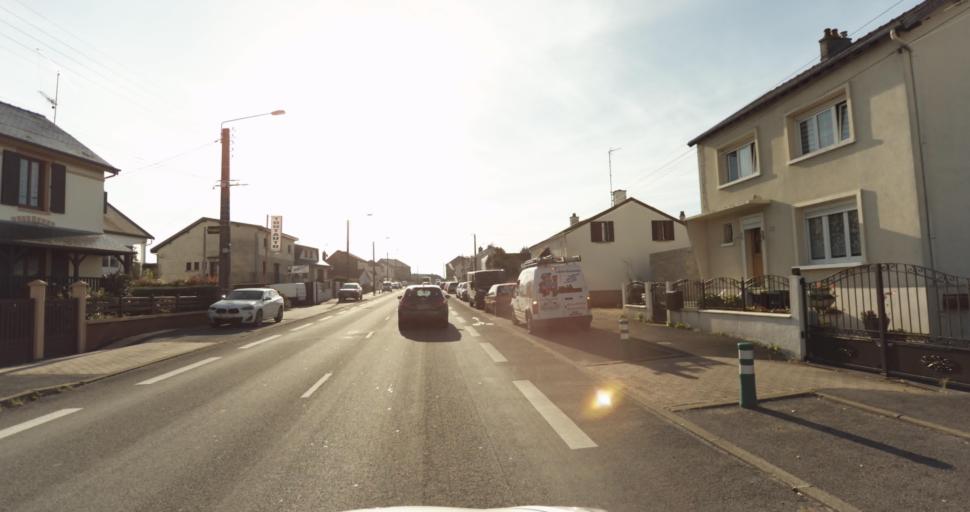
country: FR
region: Champagne-Ardenne
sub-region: Departement des Ardennes
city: Villers-Semeuse
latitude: 49.7409
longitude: 4.7445
